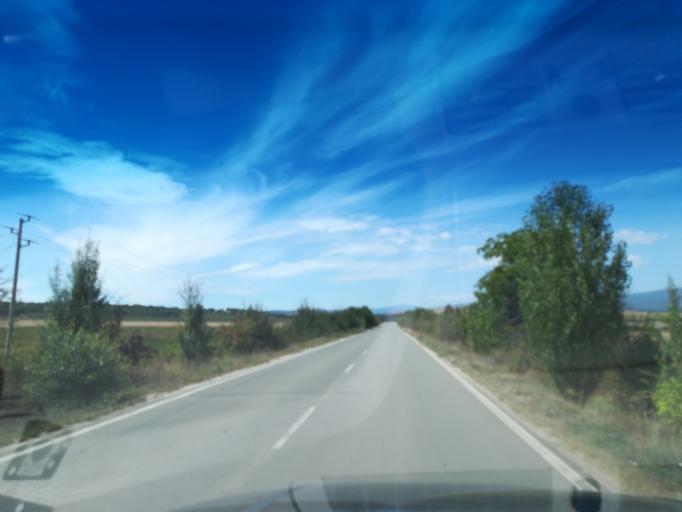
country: BG
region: Plovdiv
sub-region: Obshtina Suedinenie
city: Suedinenie
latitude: 42.4042
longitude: 24.5299
